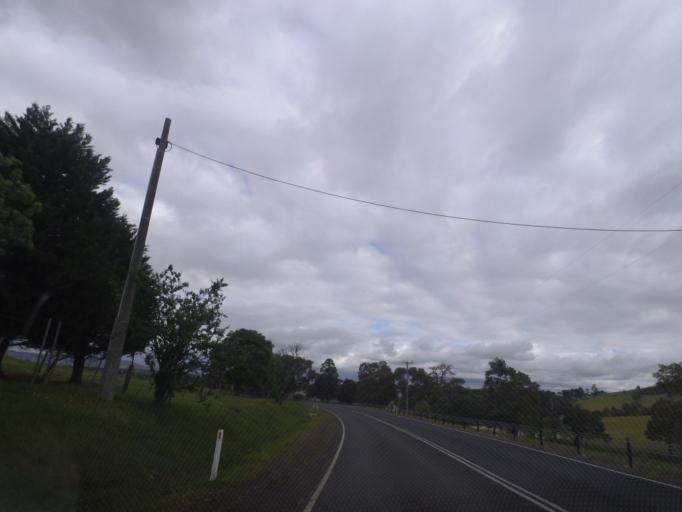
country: AU
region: Victoria
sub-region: Whittlesea
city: Whittlesea
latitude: -37.4923
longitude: 145.0632
